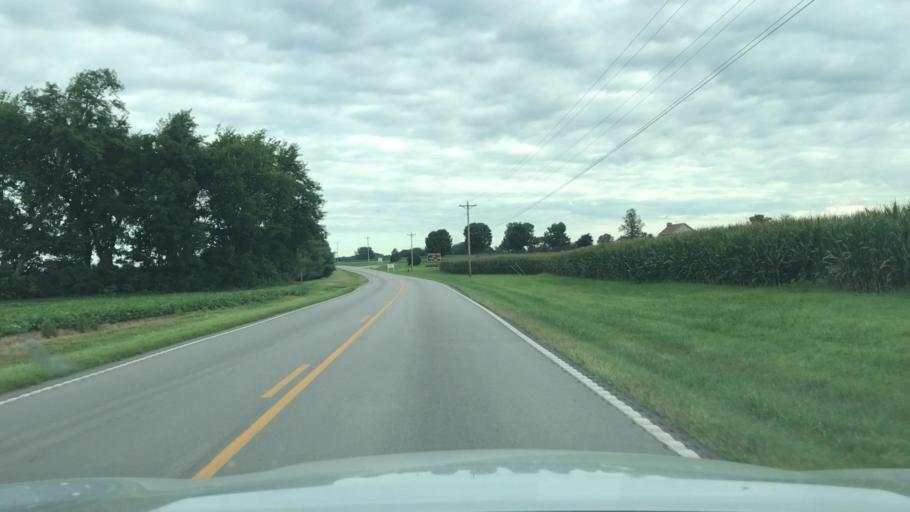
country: US
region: Kentucky
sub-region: Todd County
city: Guthrie
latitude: 36.6688
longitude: -87.1977
